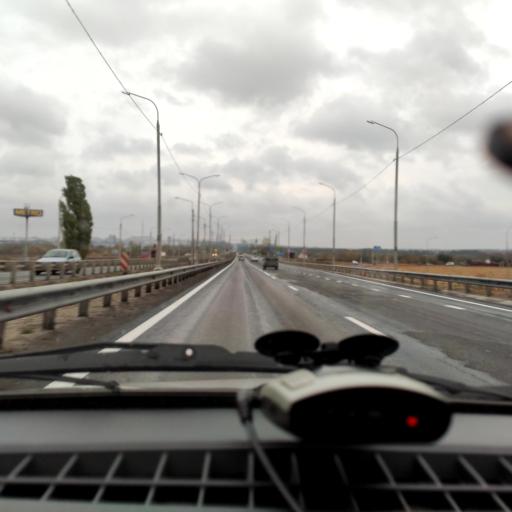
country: RU
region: Voronezj
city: Pridonskoy
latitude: 51.6517
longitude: 39.0597
